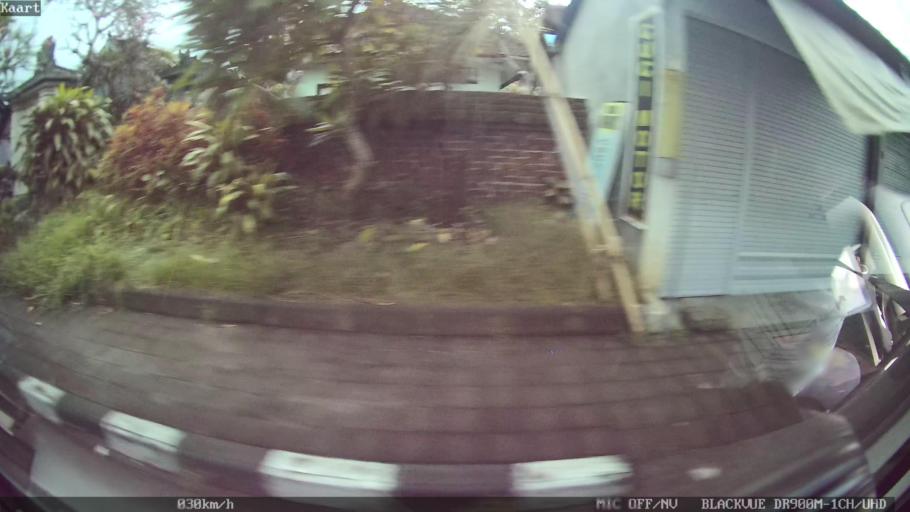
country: ID
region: Bali
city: Banjar Cemenggon
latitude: -8.5420
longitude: 115.1986
